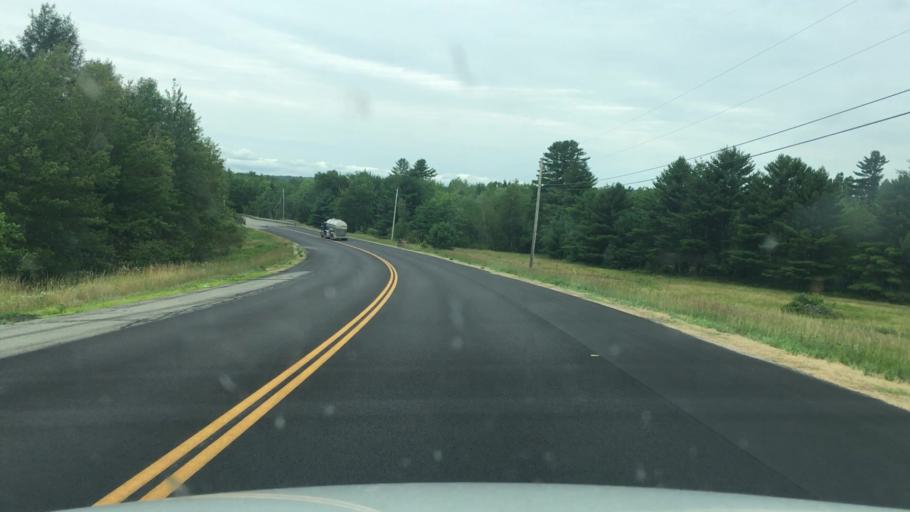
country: US
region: Maine
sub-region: Waldo County
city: Palermo
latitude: 44.3799
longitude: -69.3997
